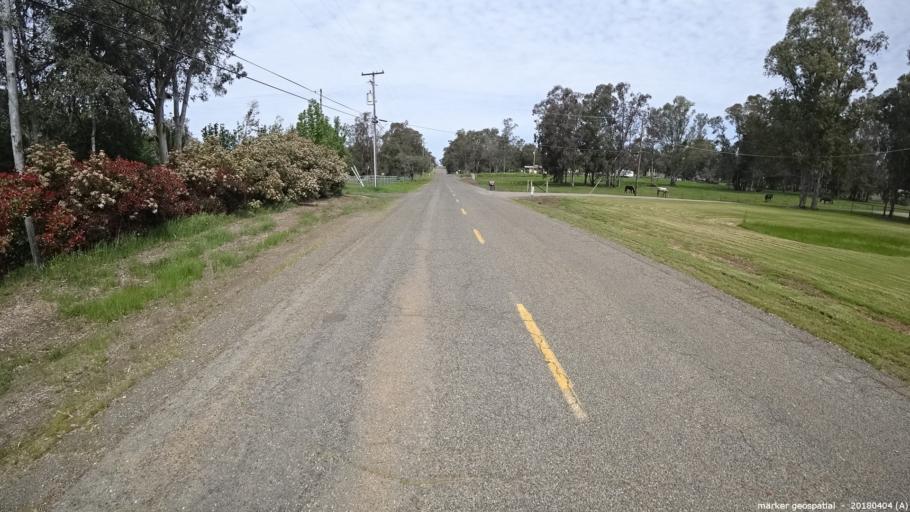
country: US
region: California
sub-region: Sacramento County
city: Clay
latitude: 38.3259
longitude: -121.1452
